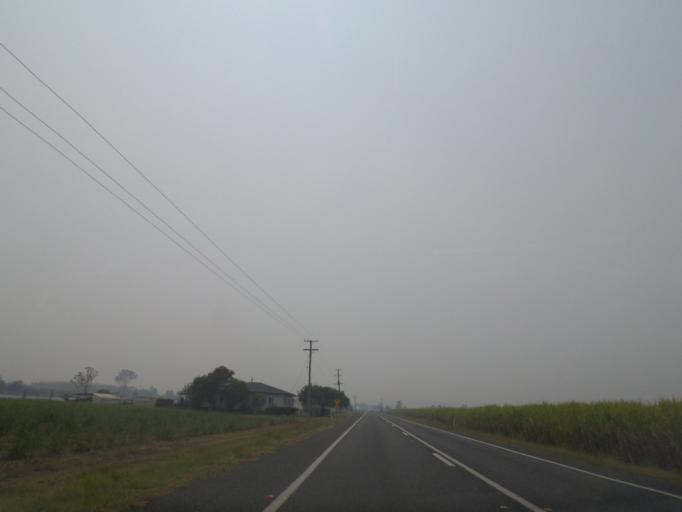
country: AU
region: New South Wales
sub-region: Clarence Valley
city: Maclean
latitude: -29.5650
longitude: 153.1152
